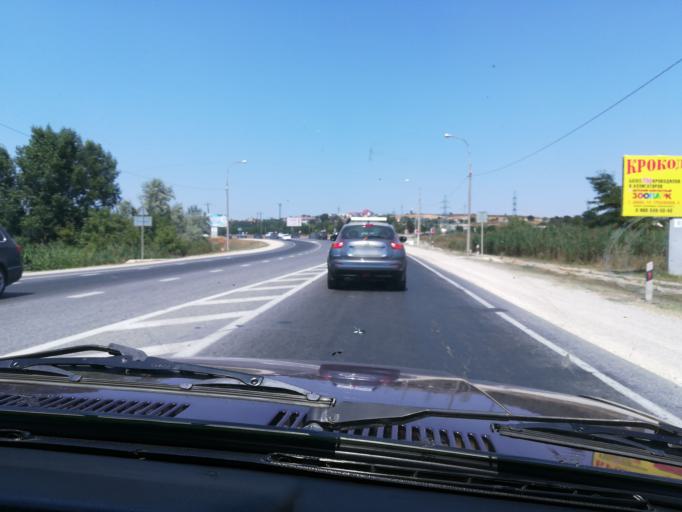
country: RU
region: Krasnodarskiy
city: Tsibanobalka
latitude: 44.9433
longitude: 37.3194
